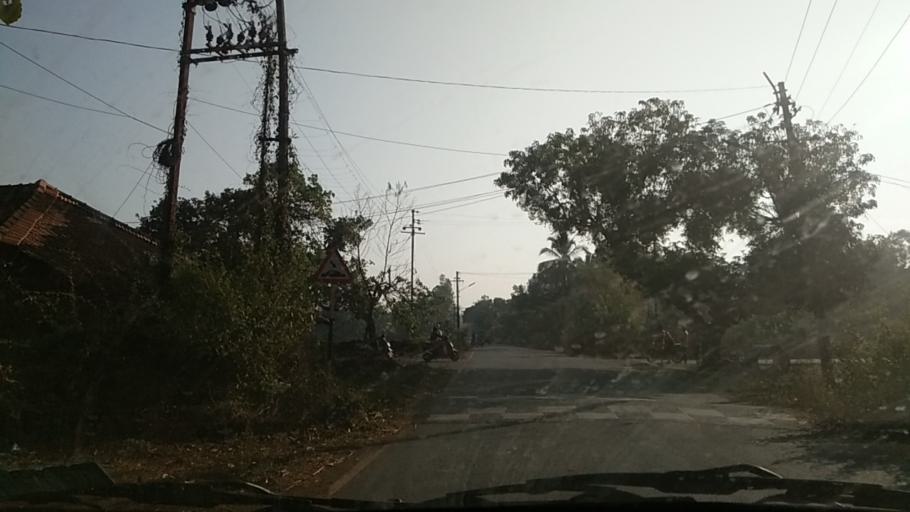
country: IN
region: Goa
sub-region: South Goa
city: Quepem
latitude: 15.1911
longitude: 74.0379
